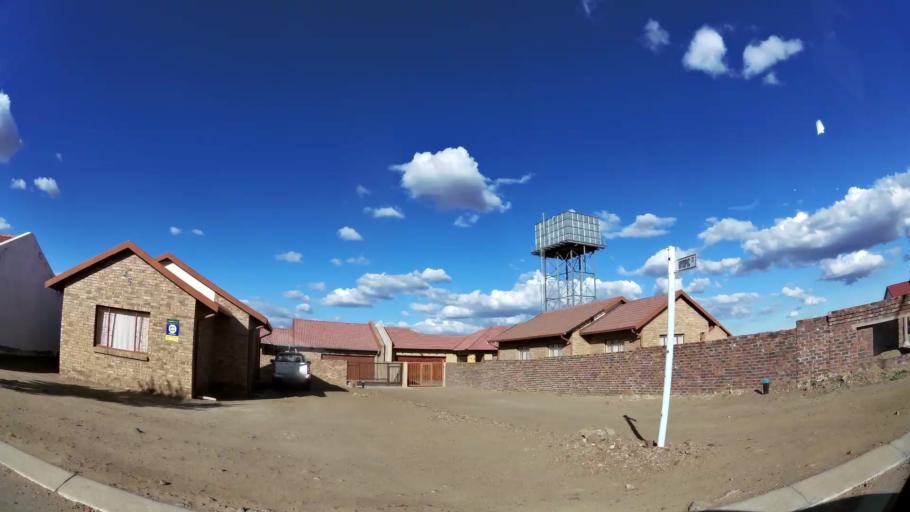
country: ZA
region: Limpopo
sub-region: Capricorn District Municipality
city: Polokwane
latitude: -23.9418
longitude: 29.4435
